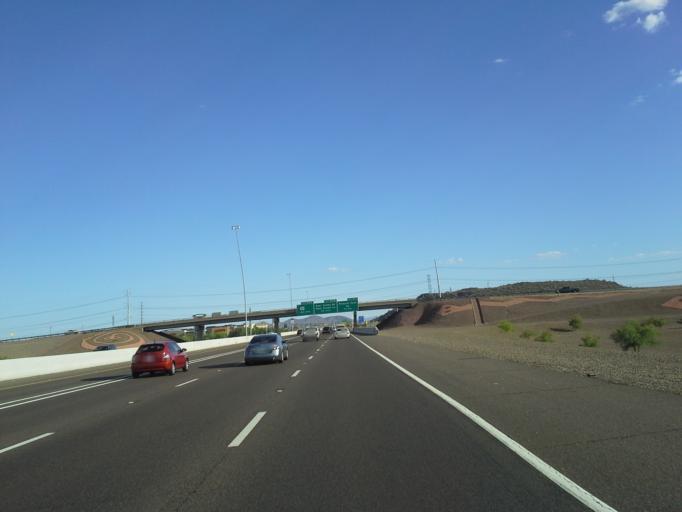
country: US
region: Arizona
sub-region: Maricopa County
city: Anthem
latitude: 33.7147
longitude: -112.1180
